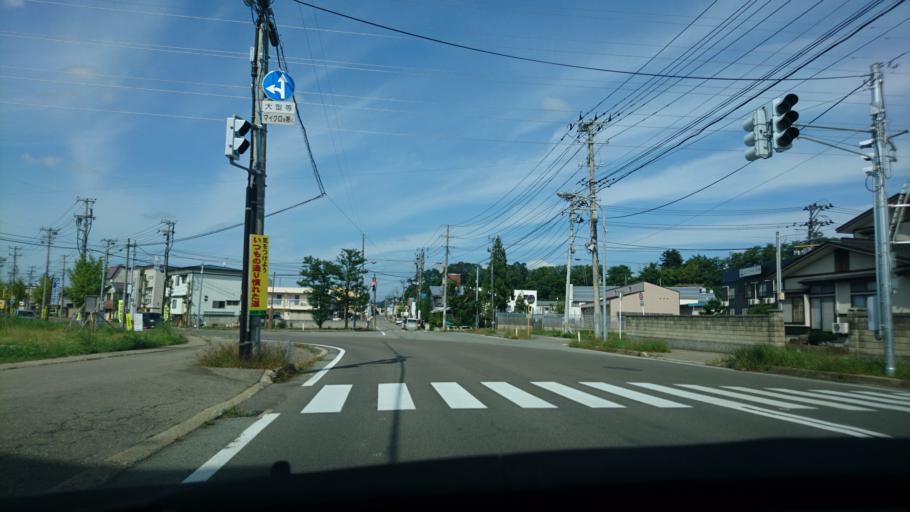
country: JP
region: Akita
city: Yokotemachi
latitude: 39.3023
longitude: 140.5655
